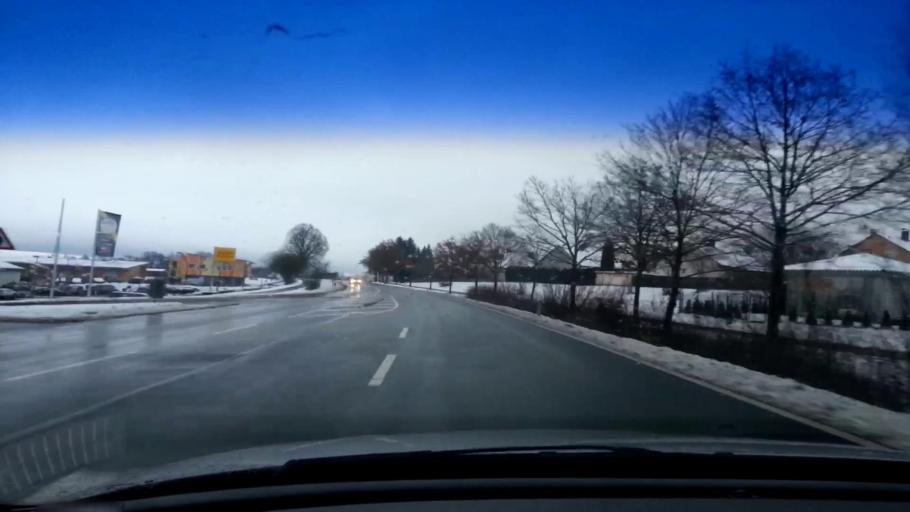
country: DE
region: Bavaria
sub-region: Upper Franconia
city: Memmelsdorf
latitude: 49.9104
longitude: 10.9803
